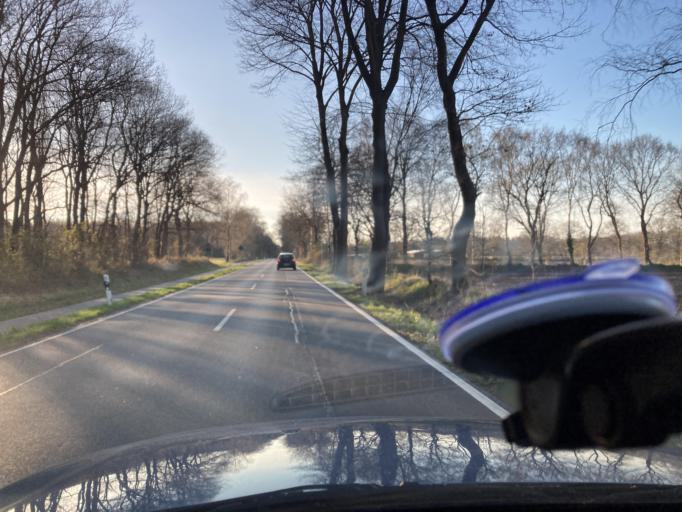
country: DE
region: Schleswig-Holstein
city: Weddingstedt
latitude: 54.2266
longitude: 9.1104
